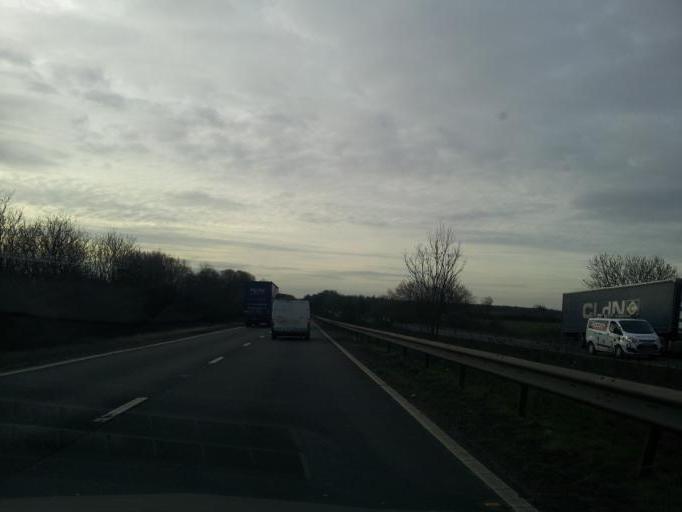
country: GB
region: England
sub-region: District of Rutland
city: Greetham
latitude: 52.7395
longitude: -0.6017
